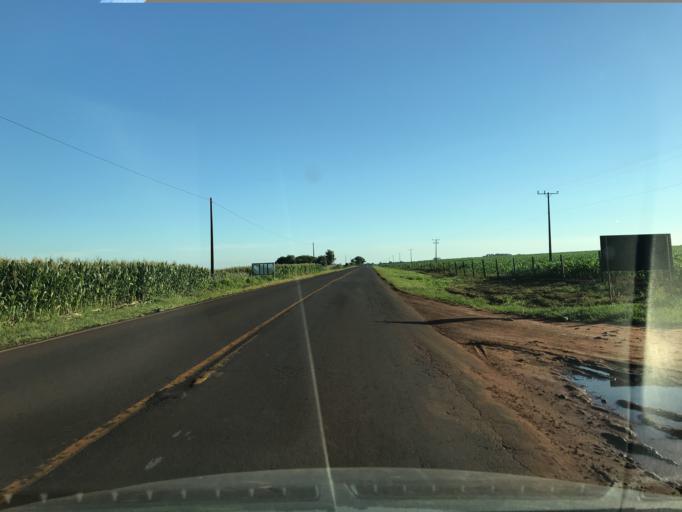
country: BR
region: Parana
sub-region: Palotina
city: Palotina
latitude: -24.1160
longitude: -53.8470
